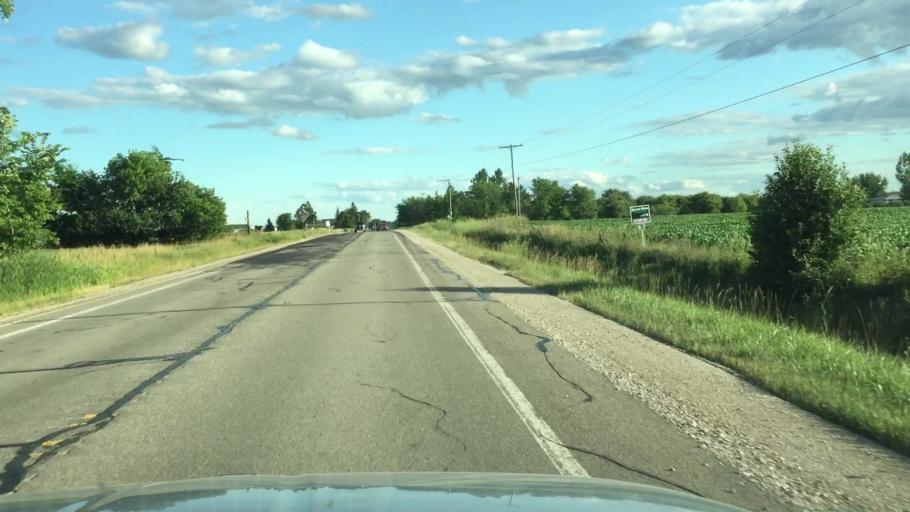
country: US
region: Michigan
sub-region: Saint Clair County
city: Yale
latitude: 43.0894
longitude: -82.7661
